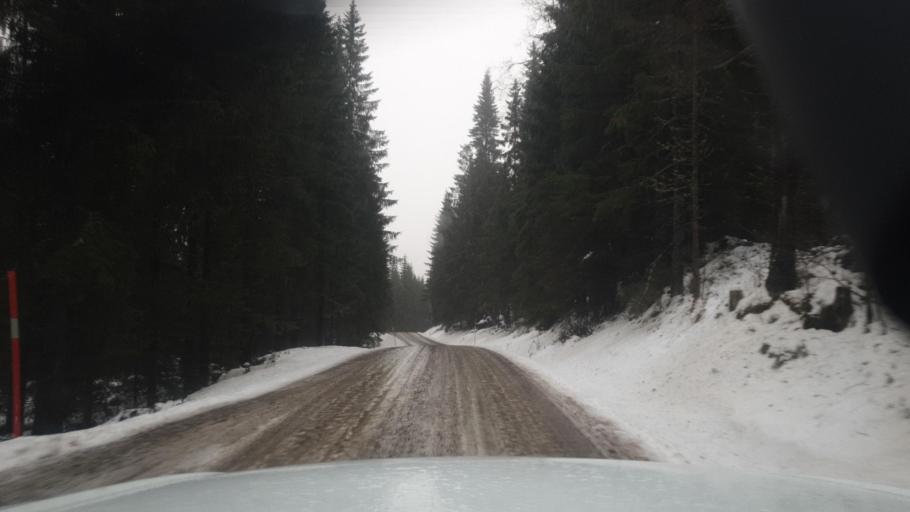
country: SE
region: Vaermland
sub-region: Eda Kommun
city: Charlottenberg
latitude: 60.0425
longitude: 12.5765
